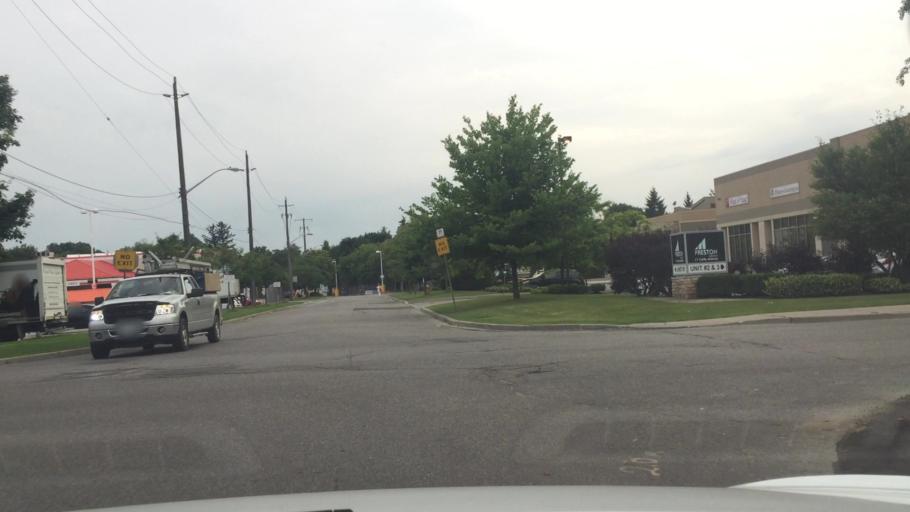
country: CA
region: Ontario
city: Scarborough
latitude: 43.7094
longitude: -79.3142
